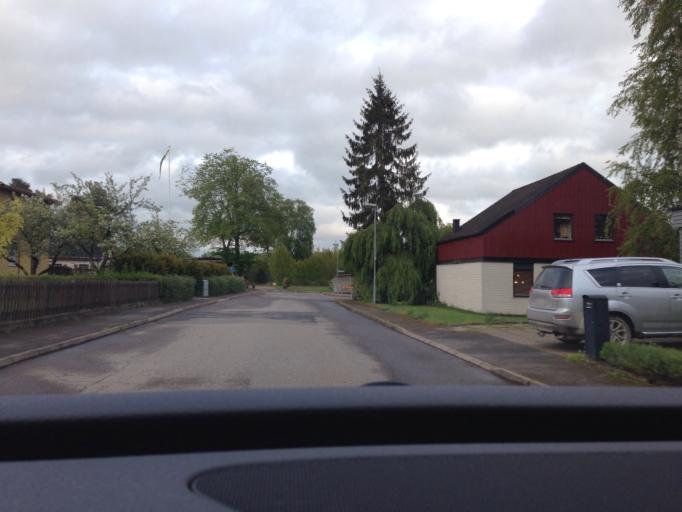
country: SE
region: Vaestra Goetaland
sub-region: Skovde Kommun
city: Skoevde
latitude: 58.4131
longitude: 13.8742
